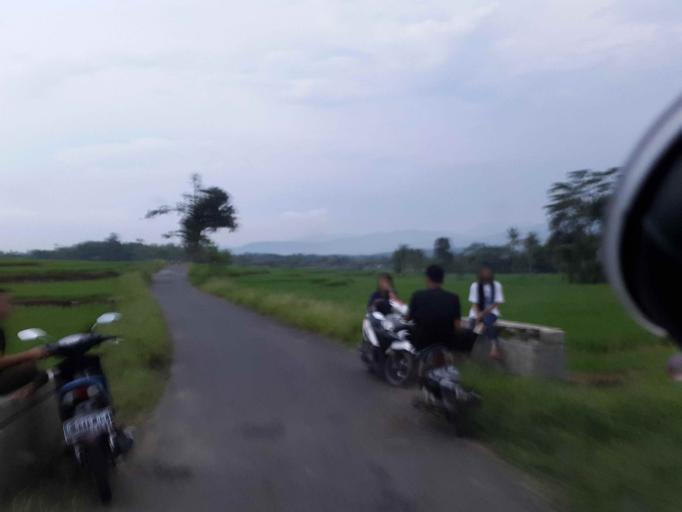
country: ID
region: Central Java
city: Randudongkal
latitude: -7.0754
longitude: 109.3343
